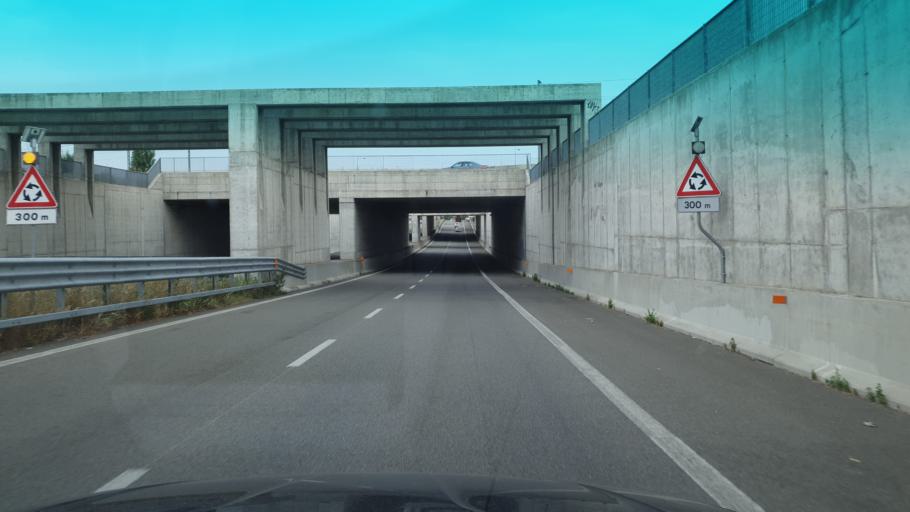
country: IT
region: Lombardy
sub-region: Provincia di Bergamo
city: Casirate d'Adda
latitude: 45.5093
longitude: 9.5558
